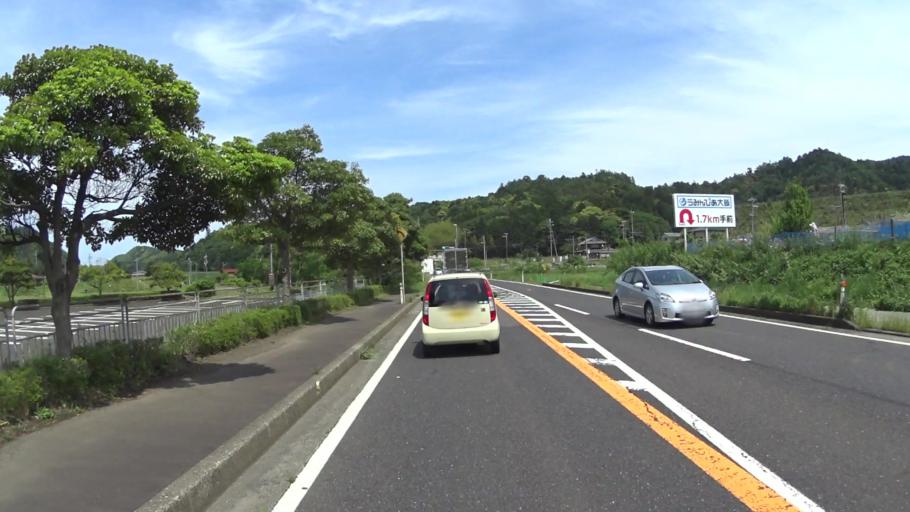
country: JP
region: Fukui
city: Obama
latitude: 35.4780
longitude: 135.6518
